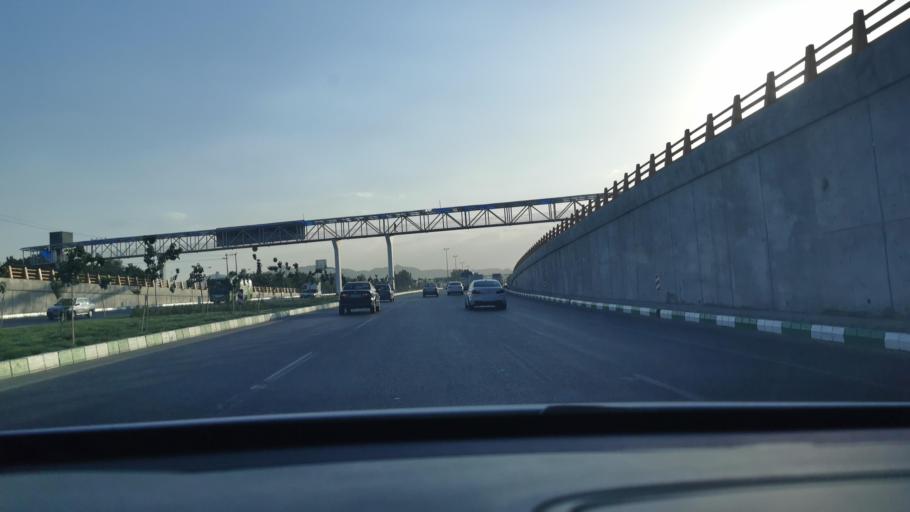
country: IR
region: Razavi Khorasan
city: Mashhad
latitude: 36.2595
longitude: 59.6437
